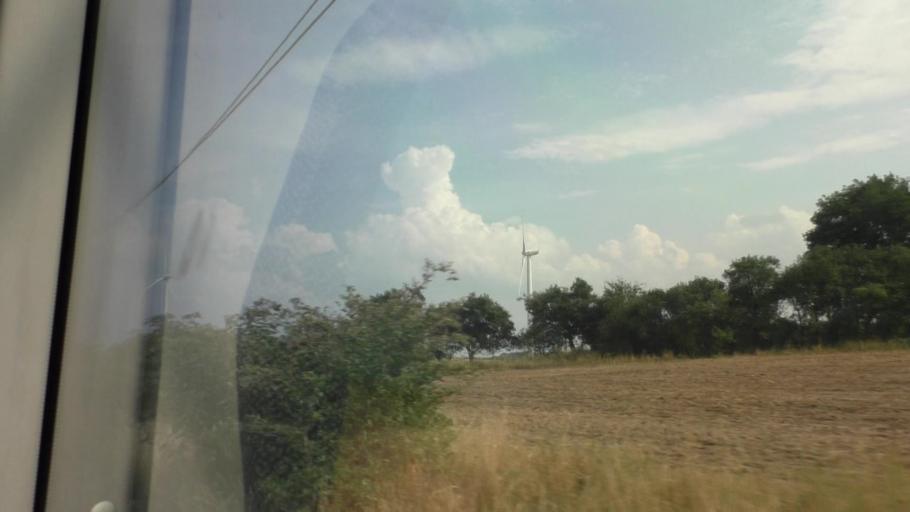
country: DE
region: Brandenburg
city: Diensdorf-Radlow
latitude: 52.2003
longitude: 14.0656
